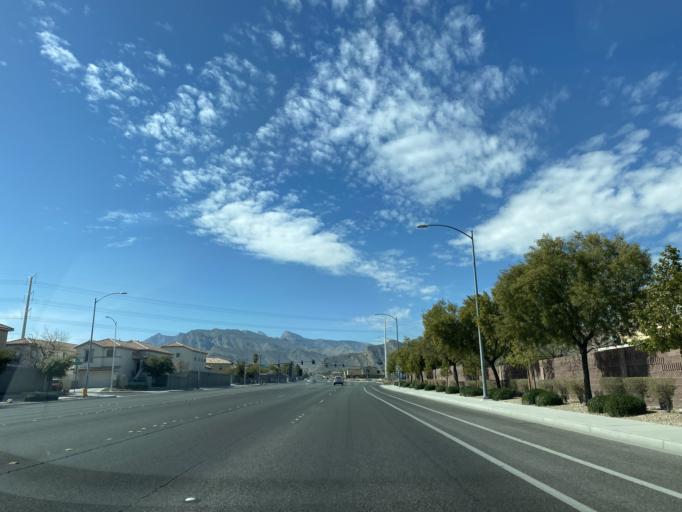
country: US
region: Nevada
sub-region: Clark County
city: Summerlin South
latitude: 36.2337
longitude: -115.2767
